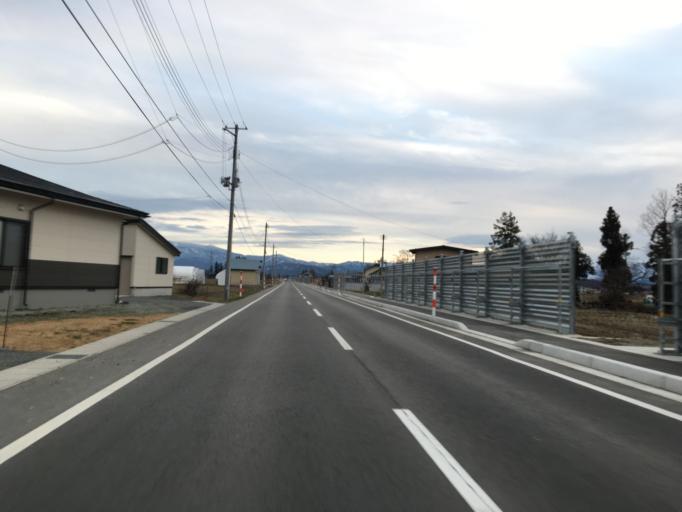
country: JP
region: Yamagata
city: Yonezawa
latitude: 38.0059
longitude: 140.0760
